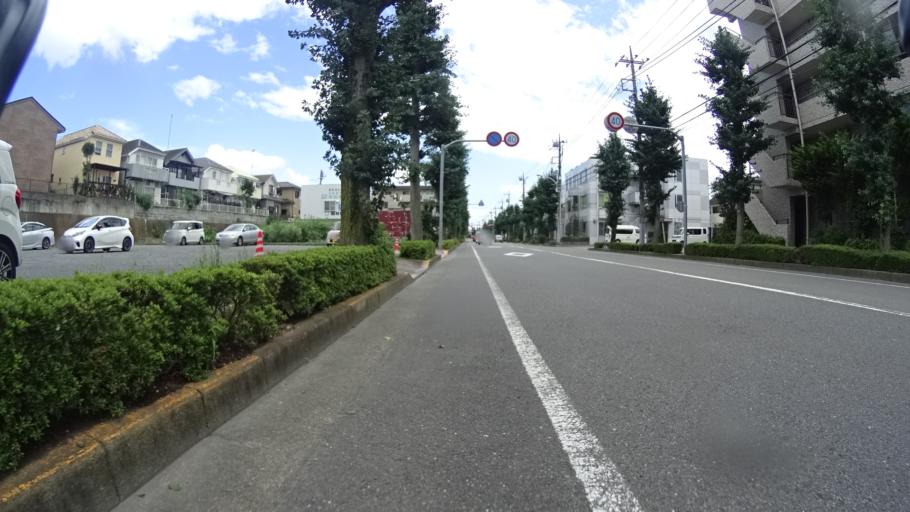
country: JP
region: Tokyo
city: Fussa
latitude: 35.7504
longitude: 139.3190
